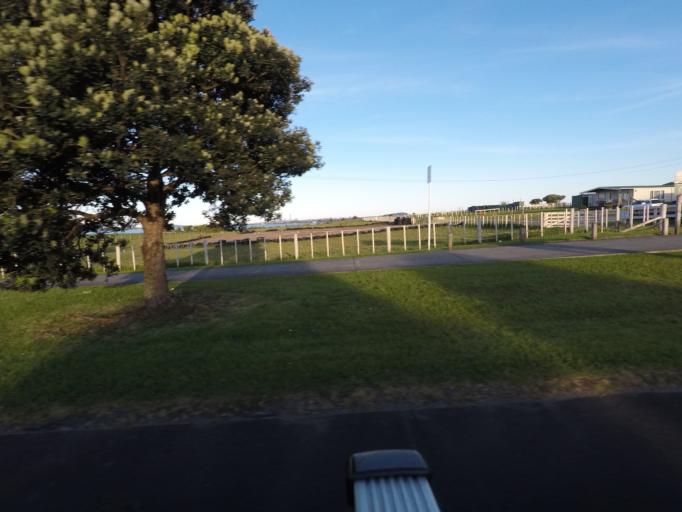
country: NZ
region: Auckland
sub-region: Auckland
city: Rosebank
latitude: -36.8531
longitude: 174.6510
